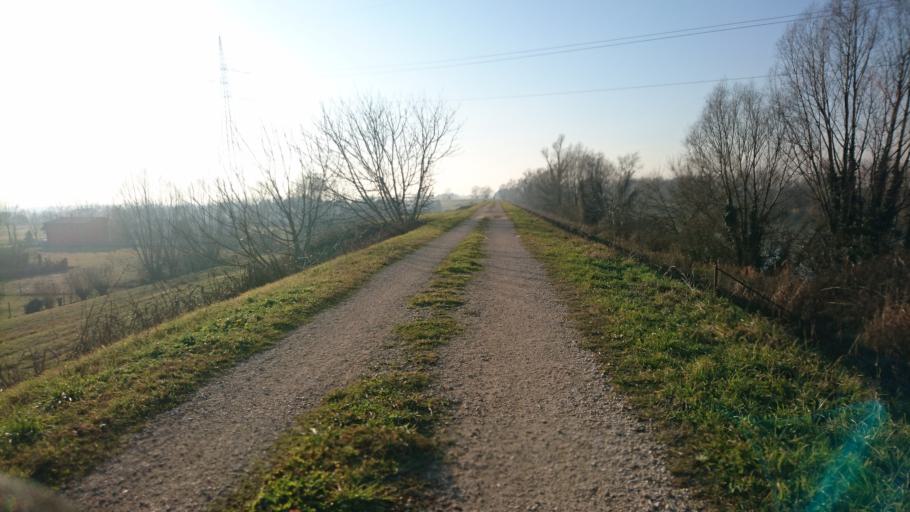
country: IT
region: Veneto
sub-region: Provincia di Rovigo
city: San Martino di Venezze
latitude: 45.1323
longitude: 11.8642
